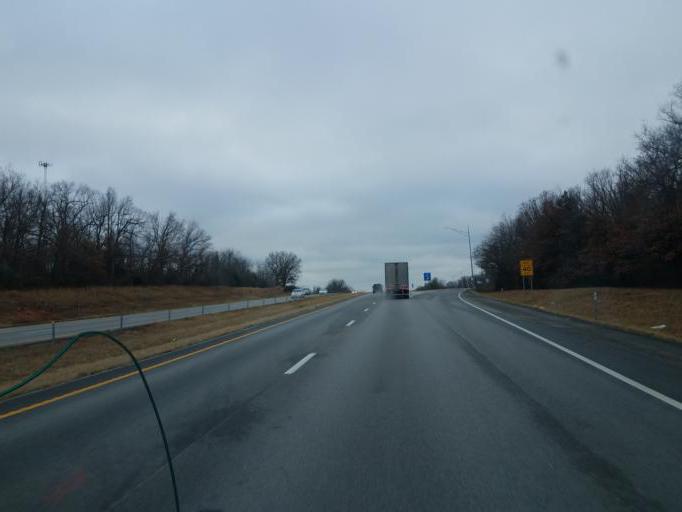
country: US
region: Missouri
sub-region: Webster County
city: Marshfield
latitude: 37.4779
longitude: -92.8553
